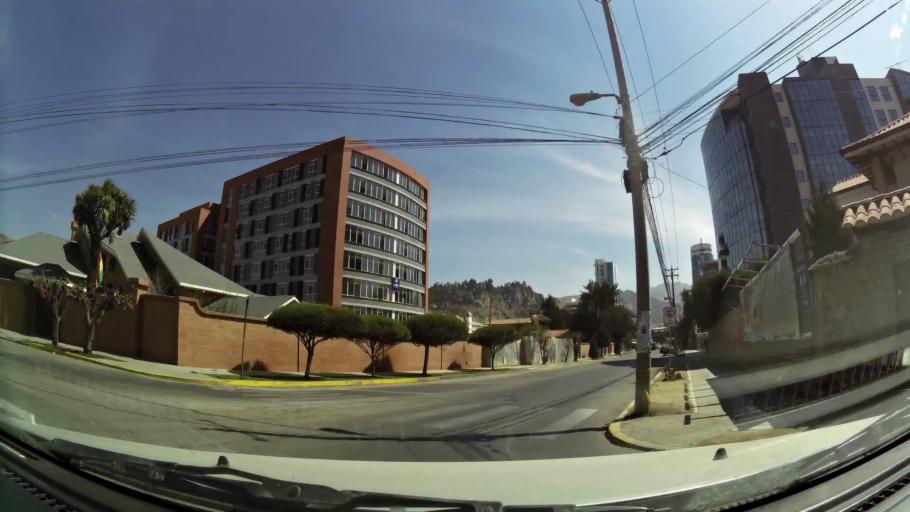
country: BO
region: La Paz
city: La Paz
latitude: -16.5408
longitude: -68.0836
